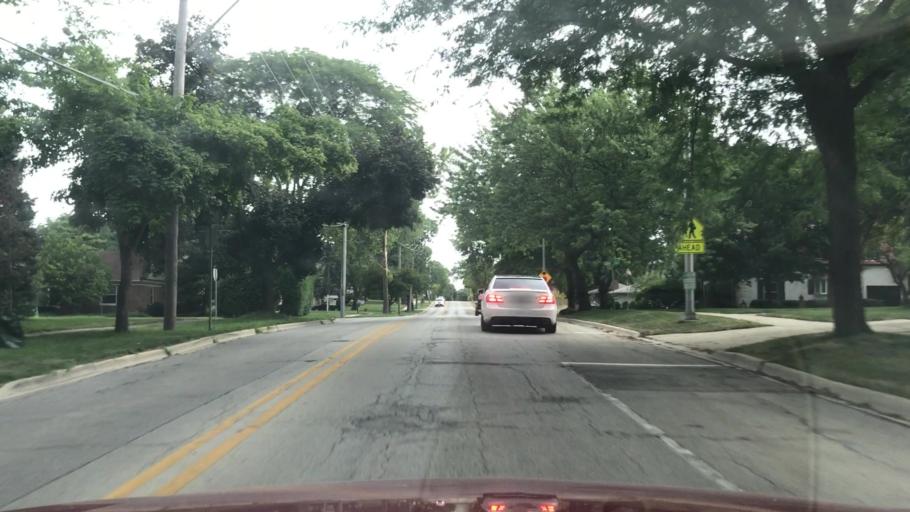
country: US
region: Illinois
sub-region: DuPage County
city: Wheaton
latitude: 41.8650
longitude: -88.0920
